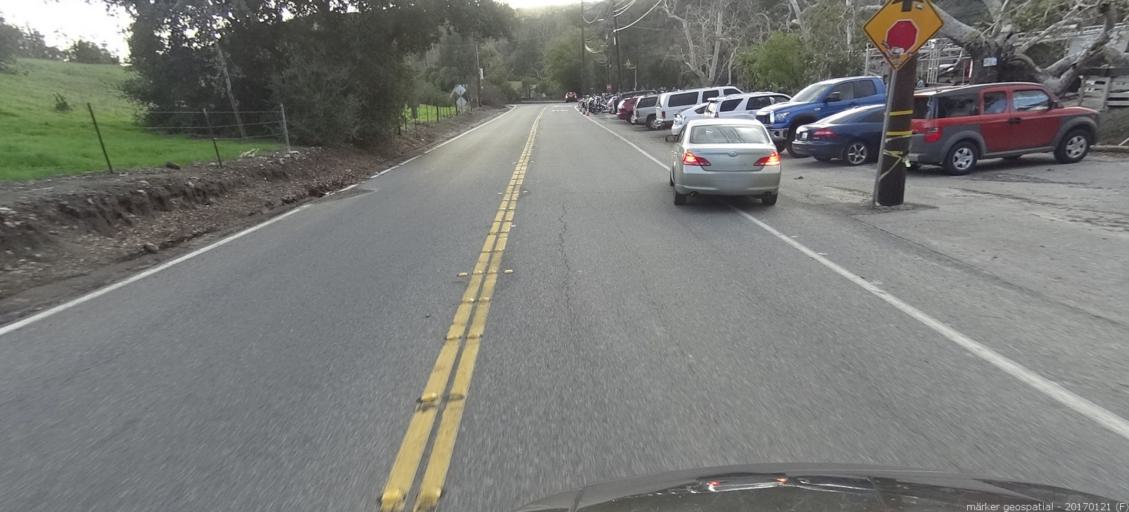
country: US
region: California
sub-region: Orange County
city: Portola Hills
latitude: 33.6840
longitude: -117.6193
